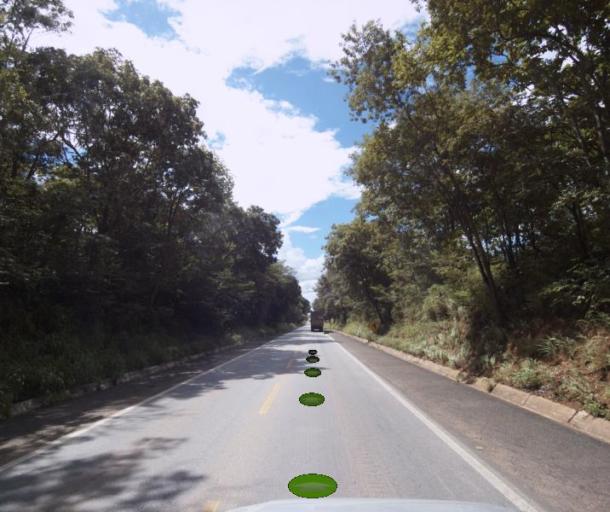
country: BR
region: Goias
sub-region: Porangatu
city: Porangatu
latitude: -13.8734
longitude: -49.0530
